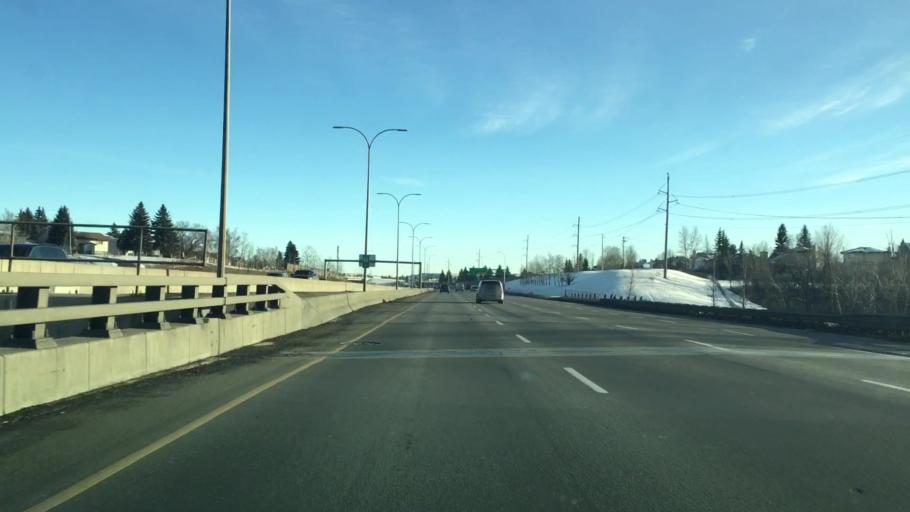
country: CA
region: Alberta
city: Calgary
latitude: 50.9859
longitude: -114.0240
